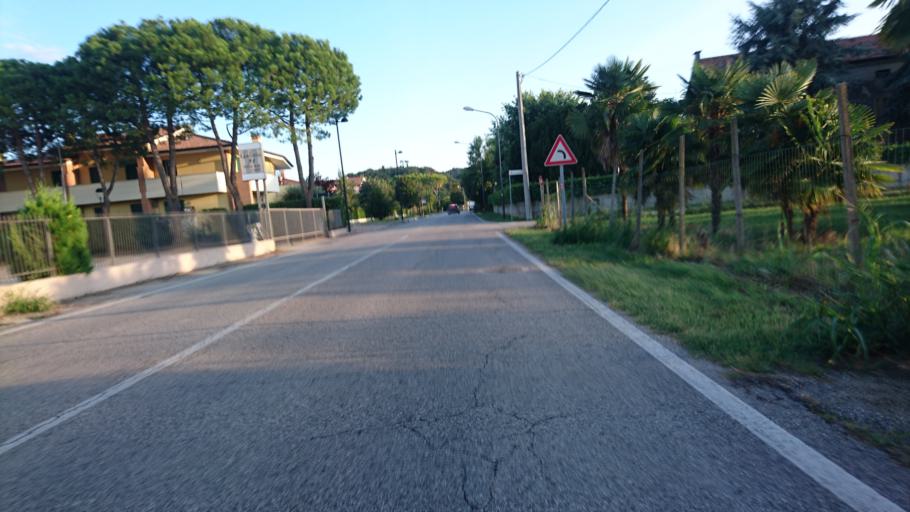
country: IT
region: Veneto
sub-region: Provincia di Padova
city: Montegrotto Terme
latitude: 45.3385
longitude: 11.7765
